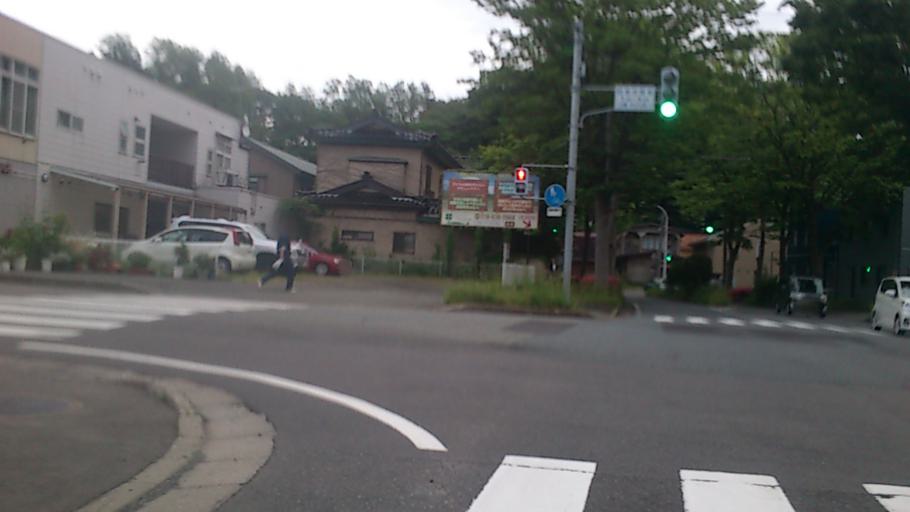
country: JP
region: Akita
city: Akita
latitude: 39.7242
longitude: 140.1206
